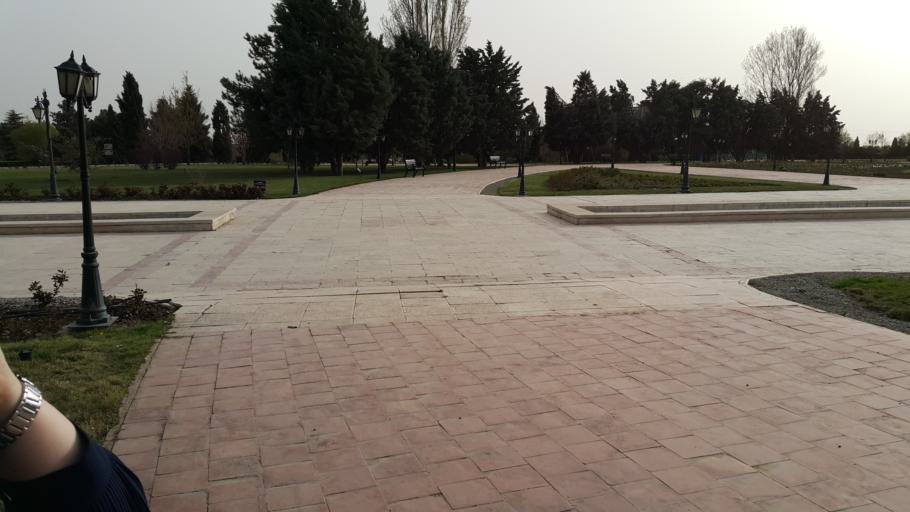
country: IR
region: Tehran
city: Shahr-e Qods
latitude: 35.7389
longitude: 51.1746
